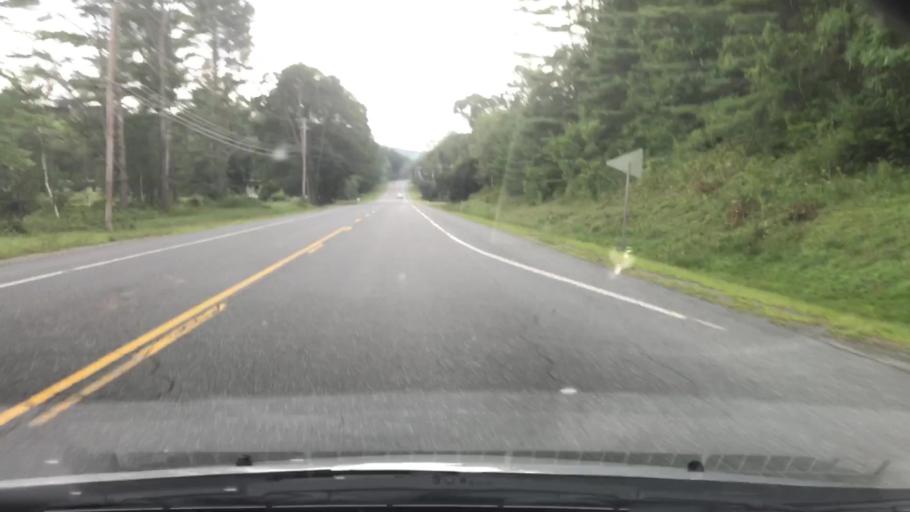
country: US
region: New Hampshire
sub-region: Grafton County
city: Lyme
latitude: 43.7792
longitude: -72.1806
